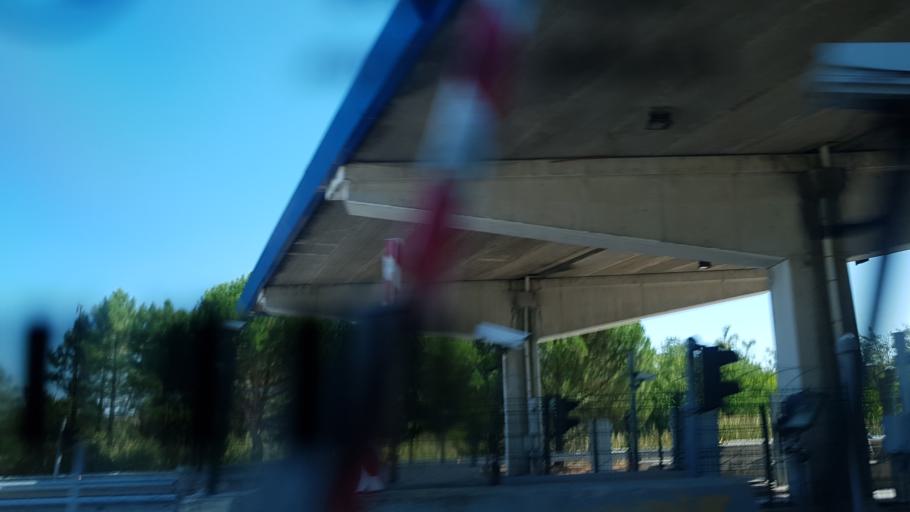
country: TR
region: Kirklareli
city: Luleburgaz
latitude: 41.4452
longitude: 27.3886
